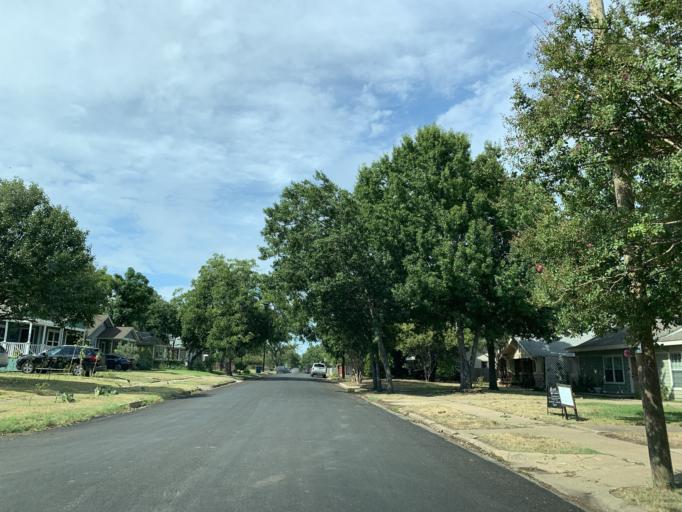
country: US
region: Texas
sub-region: Dallas County
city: Cockrell Hill
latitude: 32.7393
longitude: -96.8479
